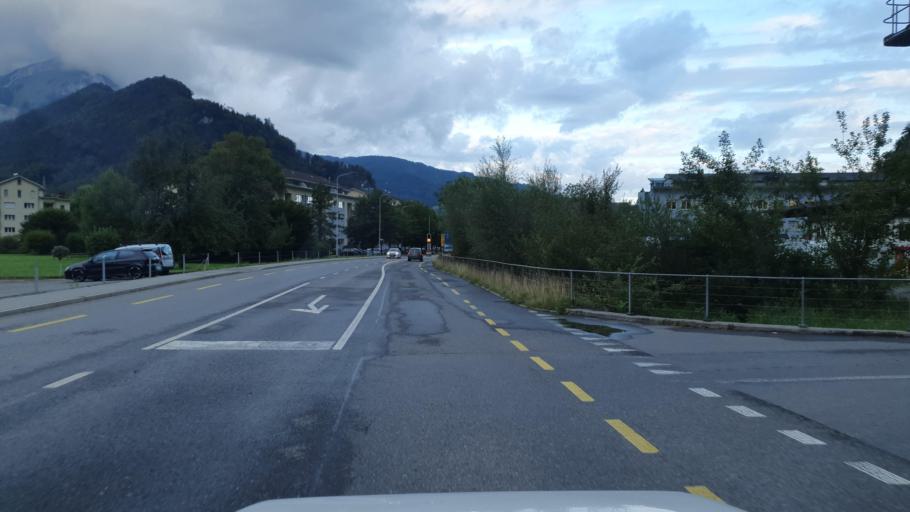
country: CH
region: Nidwalden
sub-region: Nidwalden
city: Stansstad
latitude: 46.9739
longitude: 8.3454
